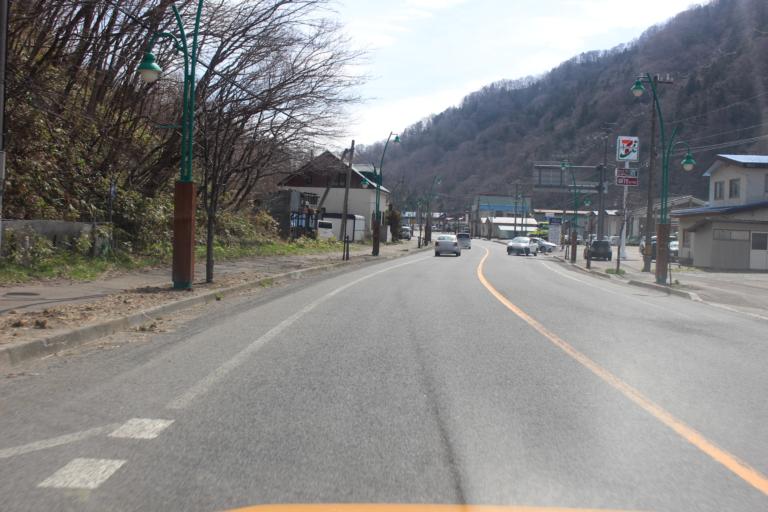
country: JP
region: Hokkaido
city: Kamiiso
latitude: 41.9151
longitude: 140.2267
